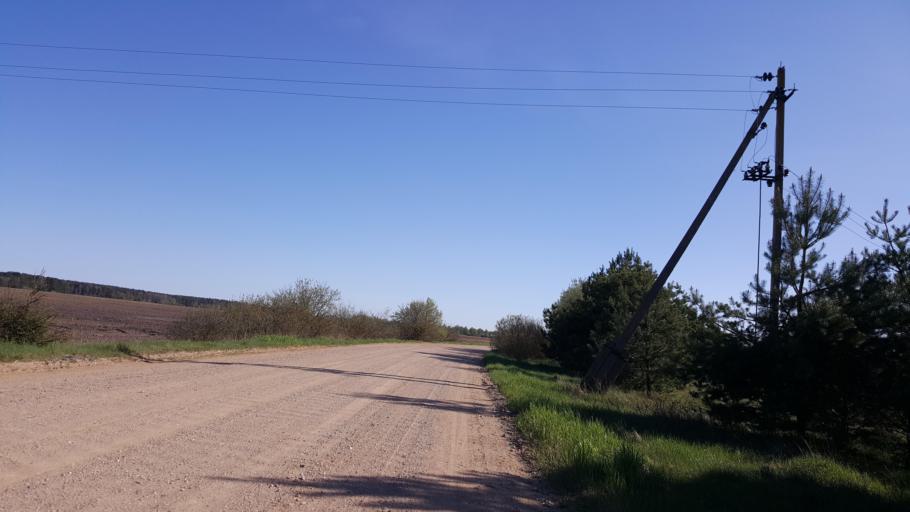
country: BY
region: Brest
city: Kamyanyets
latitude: 52.4352
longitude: 23.8854
